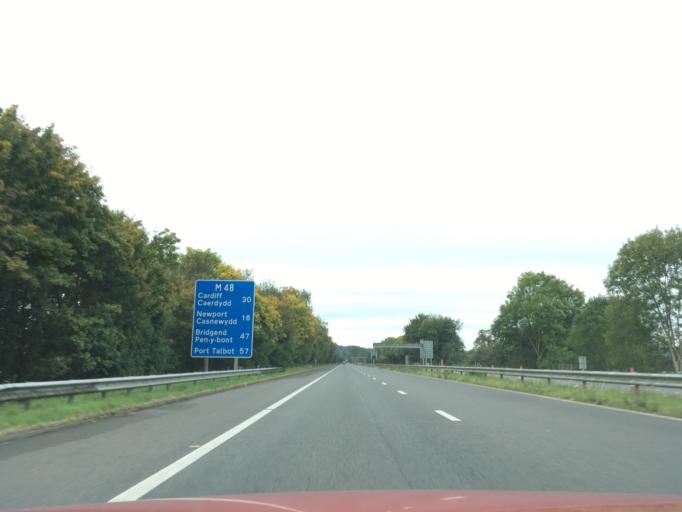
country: GB
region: Wales
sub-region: Monmouthshire
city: Chepstow
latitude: 51.6195
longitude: -2.6853
